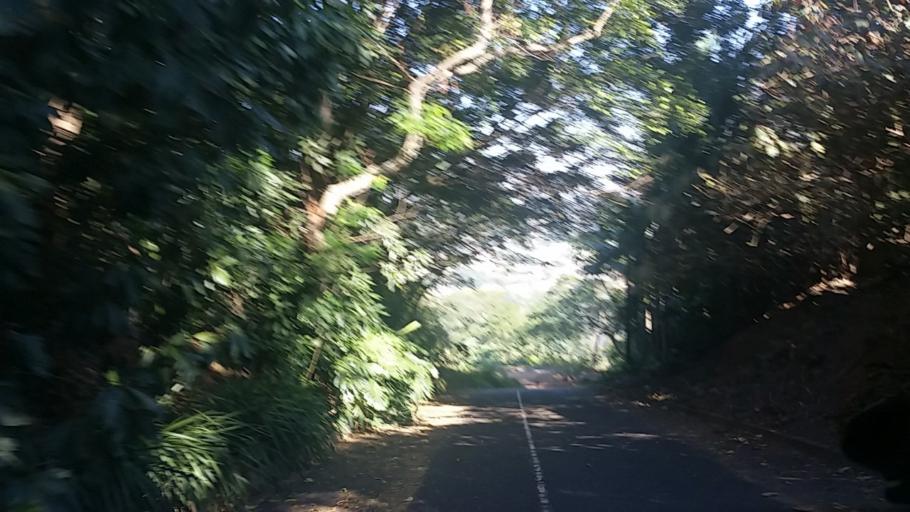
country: ZA
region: KwaZulu-Natal
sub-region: eThekwini Metropolitan Municipality
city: Berea
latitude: -29.8564
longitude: 30.9029
